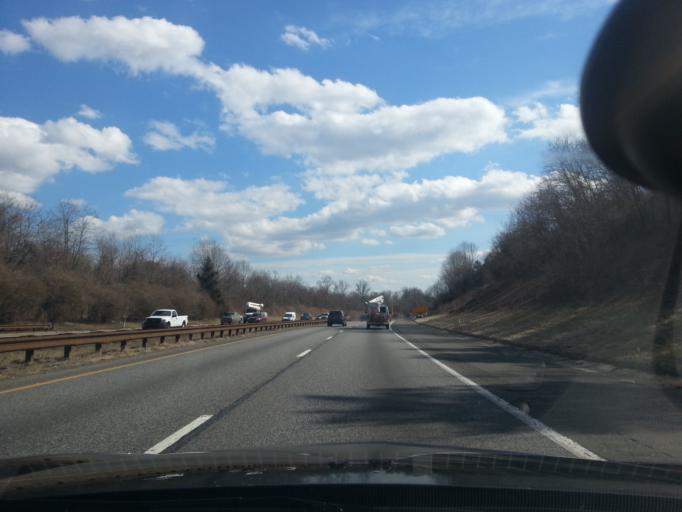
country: US
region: Pennsylvania
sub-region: Delaware County
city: Woodlyn
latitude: 39.8830
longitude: -75.3525
